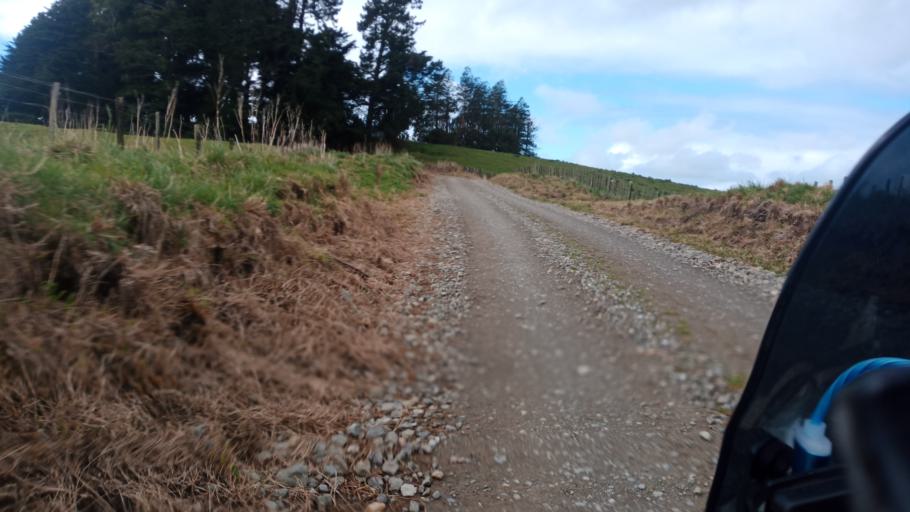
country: NZ
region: Gisborne
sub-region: Gisborne District
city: Gisborne
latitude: -38.5005
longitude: 178.2042
